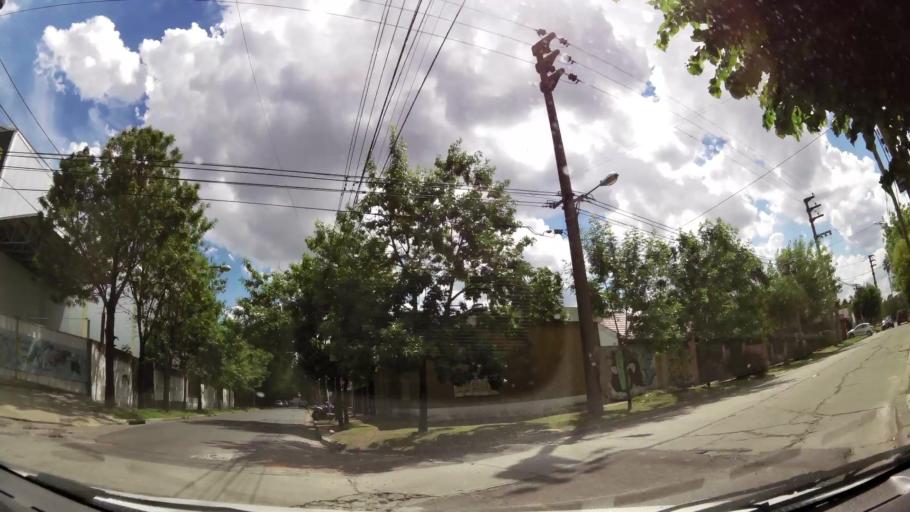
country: AR
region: Buenos Aires
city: Ituzaingo
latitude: -34.6485
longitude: -58.6744
